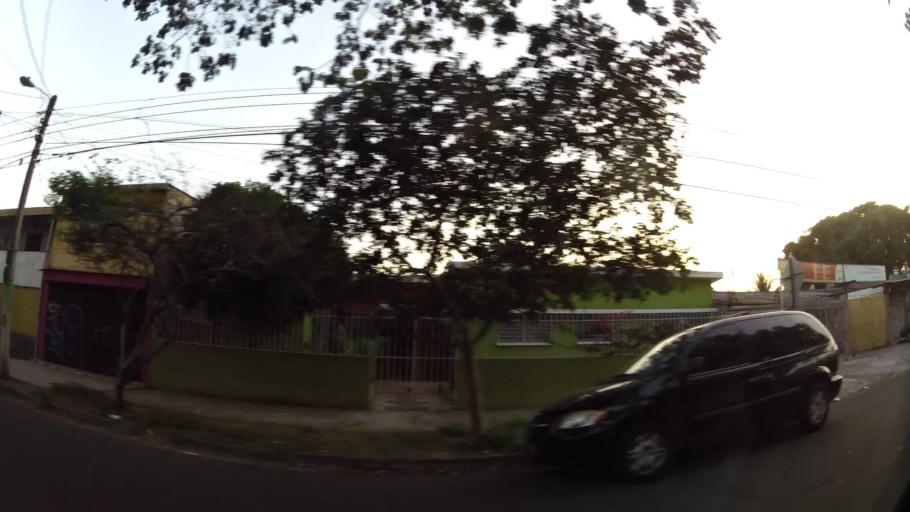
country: SV
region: San Salvador
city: Mejicanos
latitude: 13.7169
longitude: -89.2088
